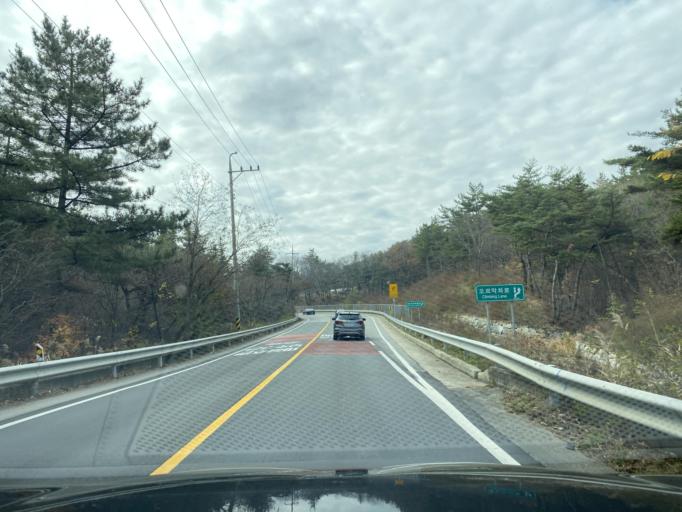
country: KR
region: Chungcheongnam-do
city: Hongsung
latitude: 36.6696
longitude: 126.6397
